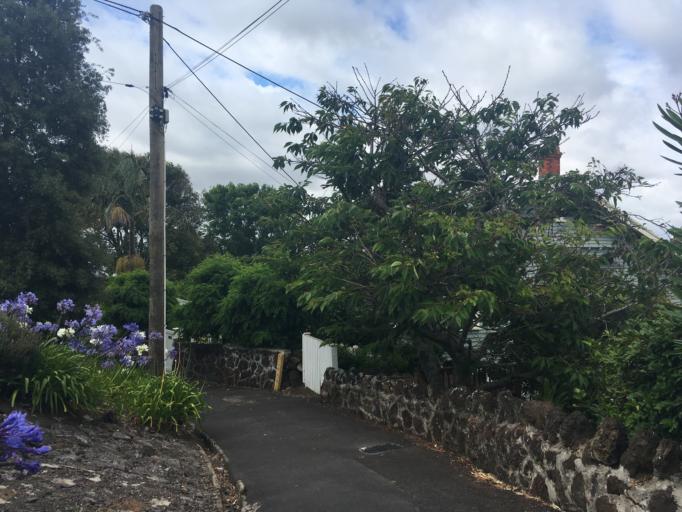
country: NZ
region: Auckland
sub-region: Auckland
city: Auckland
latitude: -36.8293
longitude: 174.8003
